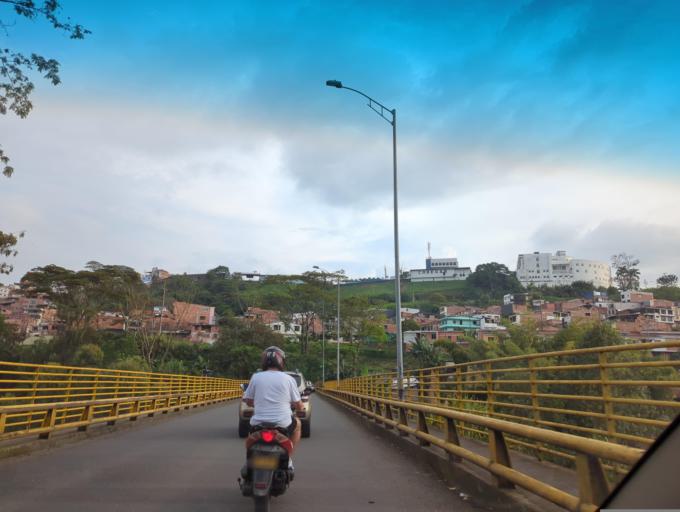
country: CO
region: Risaralda
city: Pereira
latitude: 4.8204
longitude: -75.7169
